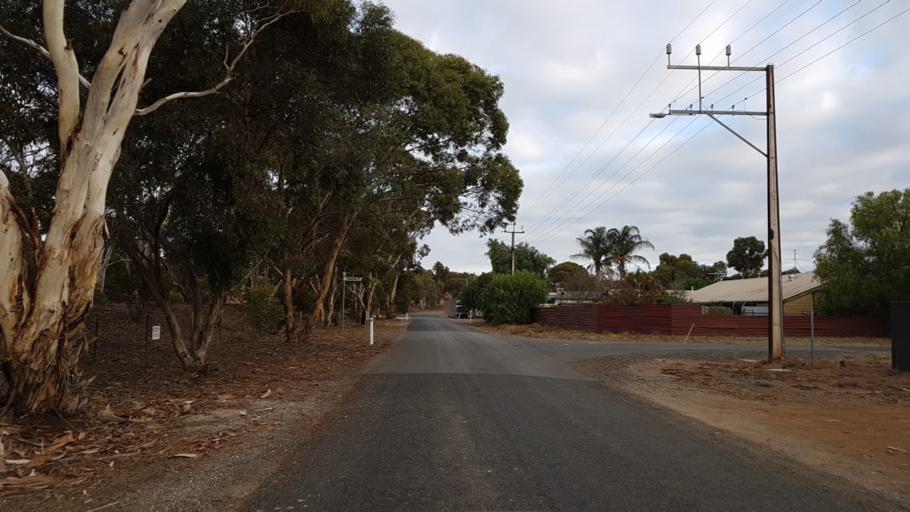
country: AU
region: South Australia
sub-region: Mount Barker
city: Callington
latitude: -35.1177
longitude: 139.0356
